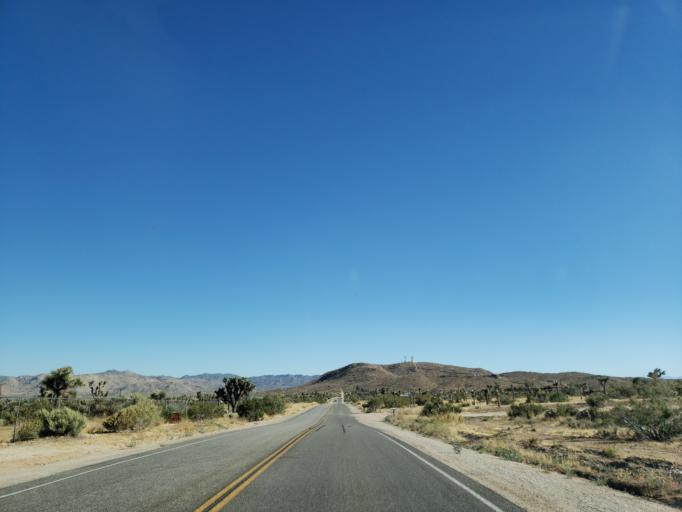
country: US
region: California
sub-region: San Bernardino County
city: Yucca Valley
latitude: 34.1701
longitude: -116.3871
